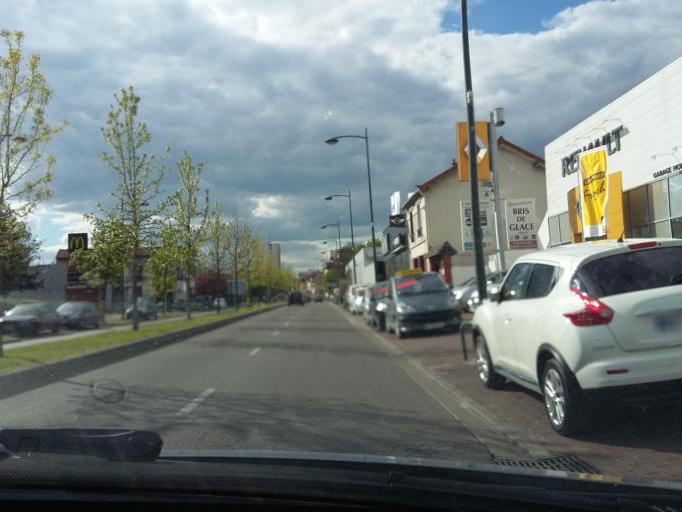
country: FR
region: Ile-de-France
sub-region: Departement du Val-d'Oise
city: Saint-Gratien
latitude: 48.9636
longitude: 2.2905
